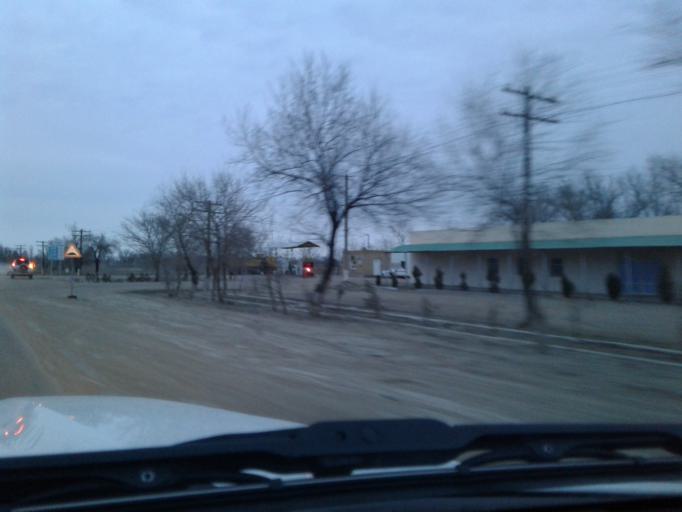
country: UZ
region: Karakalpakstan
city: Manghit
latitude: 42.0517
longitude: 59.9299
